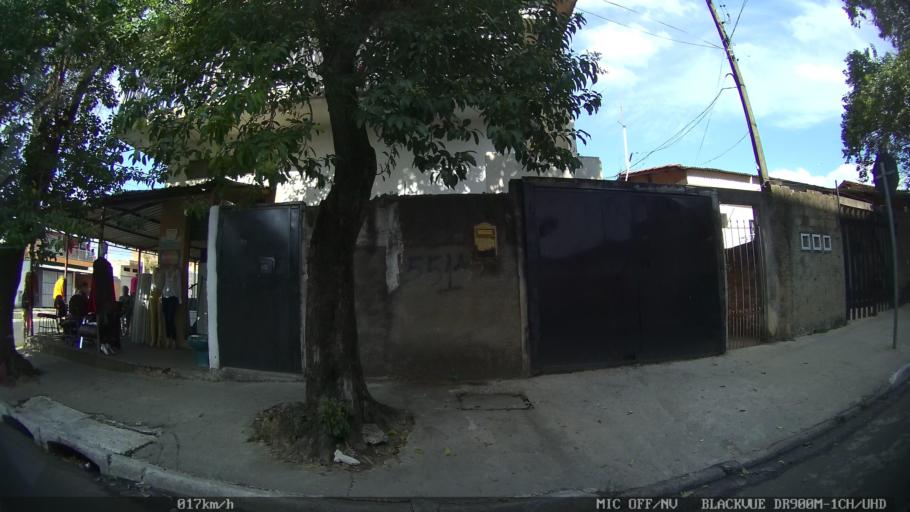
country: BR
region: Sao Paulo
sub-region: Hortolandia
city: Hortolandia
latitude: -22.9052
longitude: -47.2404
